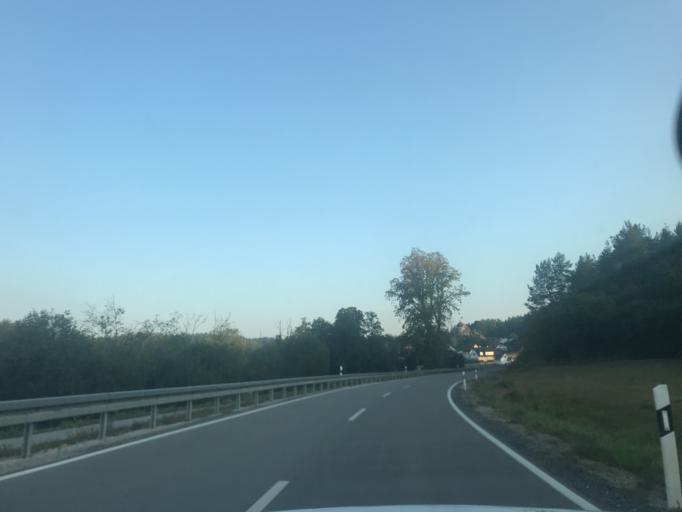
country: DE
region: Bavaria
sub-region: Upper Franconia
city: Pegnitz
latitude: 49.7224
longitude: 11.5659
